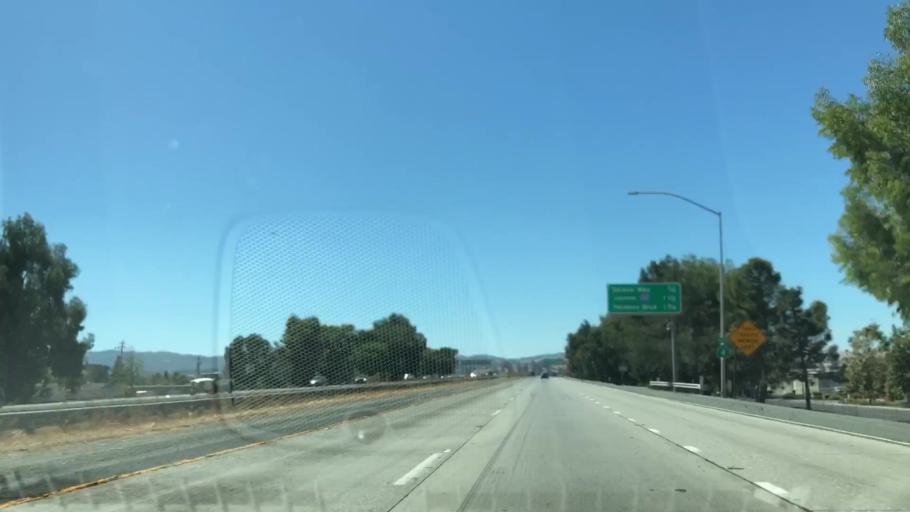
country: US
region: California
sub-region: Contra Costa County
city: Concord
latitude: 38.0038
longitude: -122.0425
